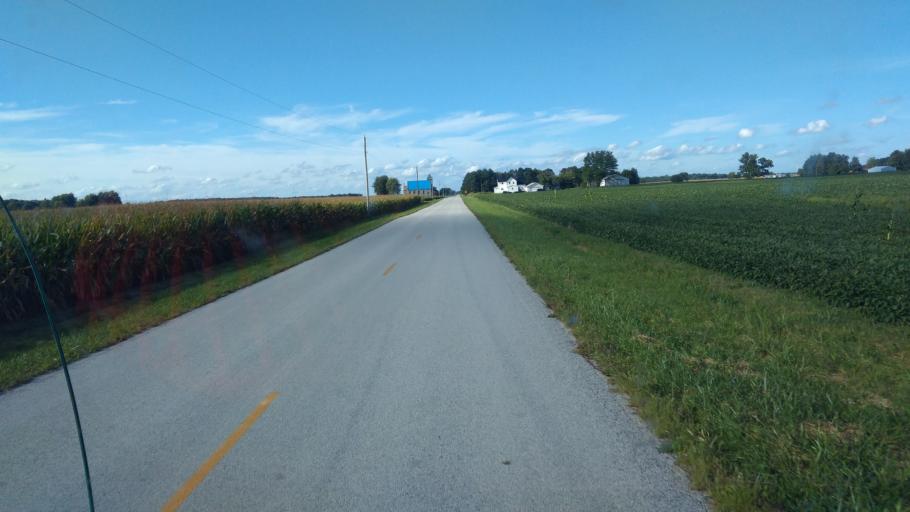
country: US
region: Ohio
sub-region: Hardin County
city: Kenton
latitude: 40.7415
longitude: -83.6907
